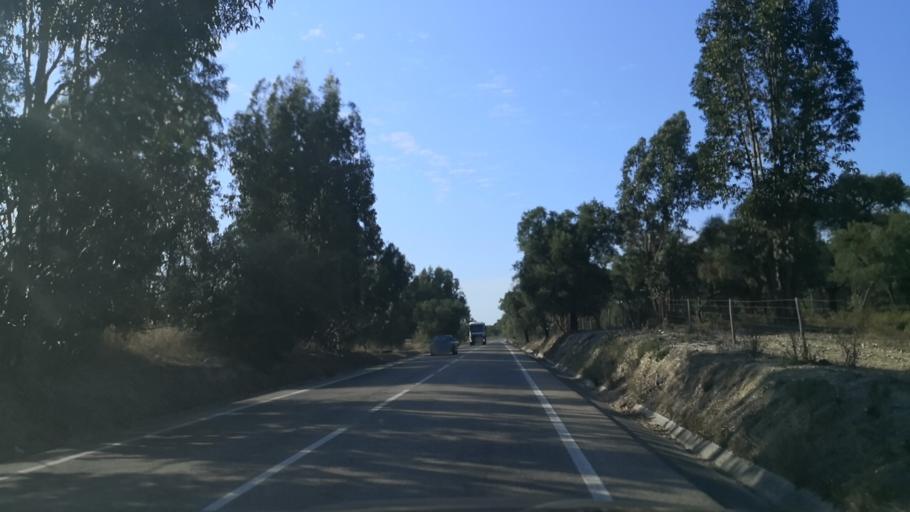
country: PT
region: Santarem
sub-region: Almeirim
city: Fazendas de Almeirim
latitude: 39.1314
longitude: -8.6076
